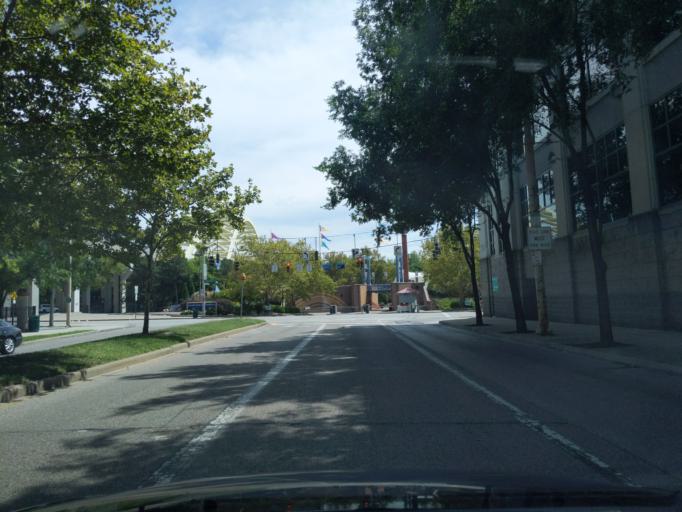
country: US
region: Kentucky
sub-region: Campbell County
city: Newport
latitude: 39.1023
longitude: -84.4996
